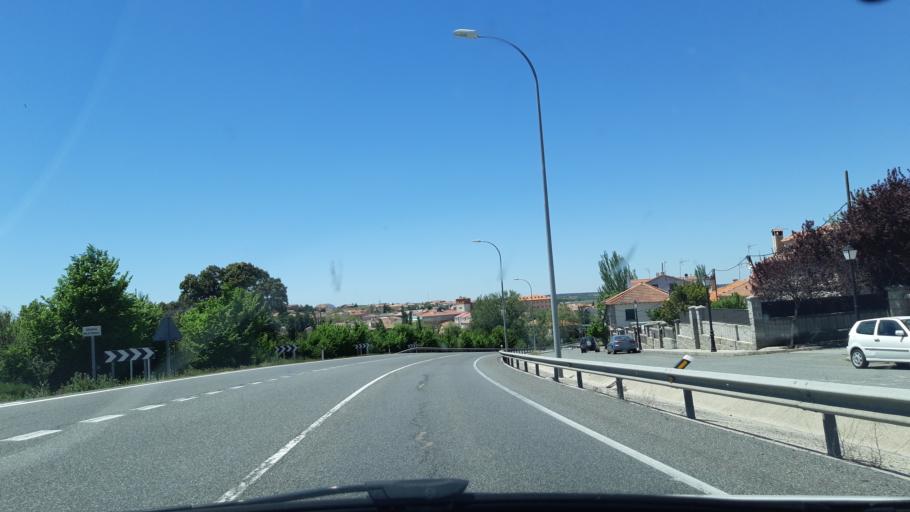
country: ES
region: Castille and Leon
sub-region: Provincia de Segovia
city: Villacastin
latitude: 40.7781
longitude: -4.4053
